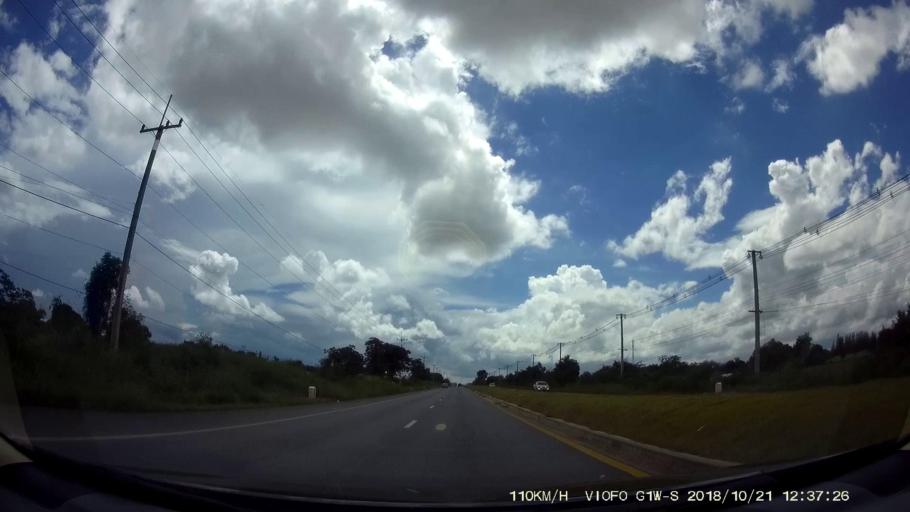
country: TH
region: Nakhon Ratchasima
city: Dan Khun Thot
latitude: 15.0693
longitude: 101.7115
